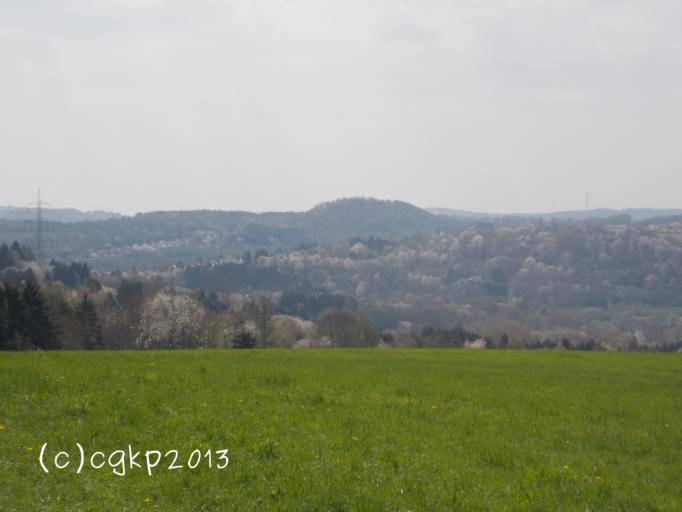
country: DE
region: Saarland
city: Hangard
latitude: 49.3900
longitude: 7.1935
